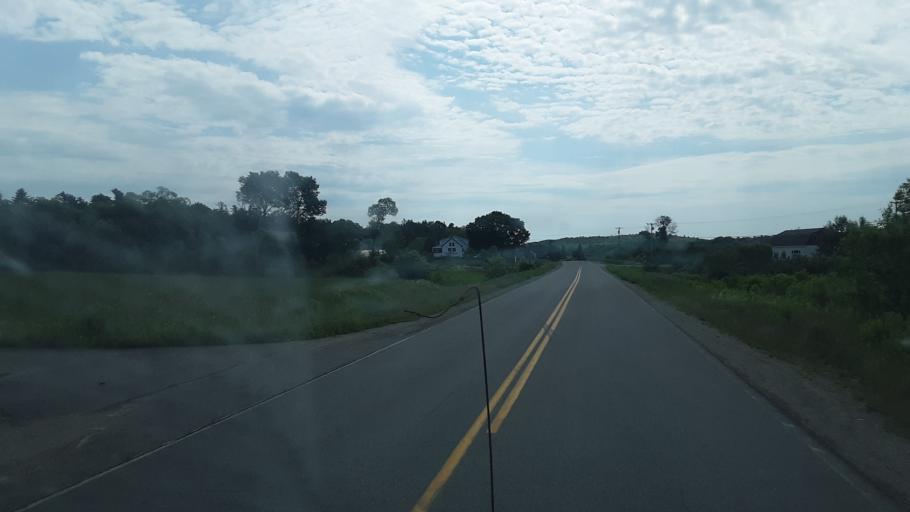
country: US
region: Maine
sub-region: Waldo County
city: Frankfort
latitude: 44.6142
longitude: -68.9285
